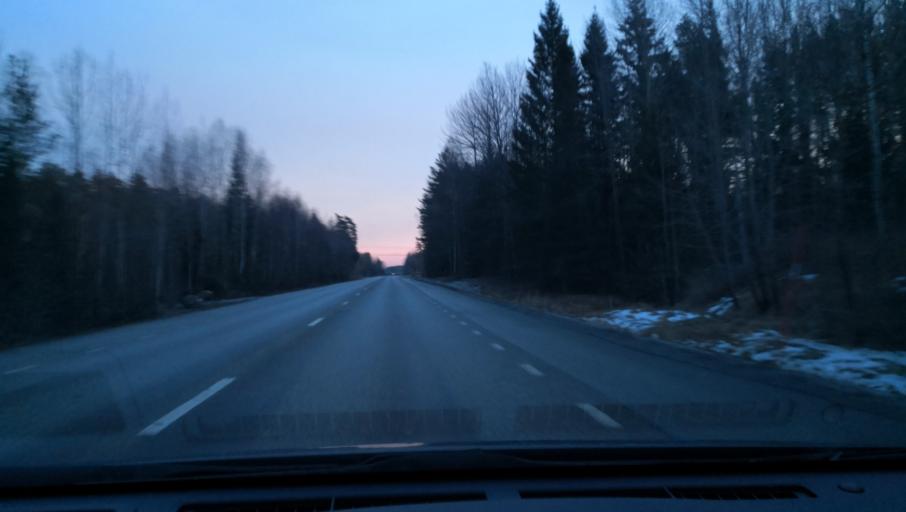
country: SE
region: OErebro
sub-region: Orebro Kommun
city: Orebro
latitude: 59.2420
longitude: 15.0897
